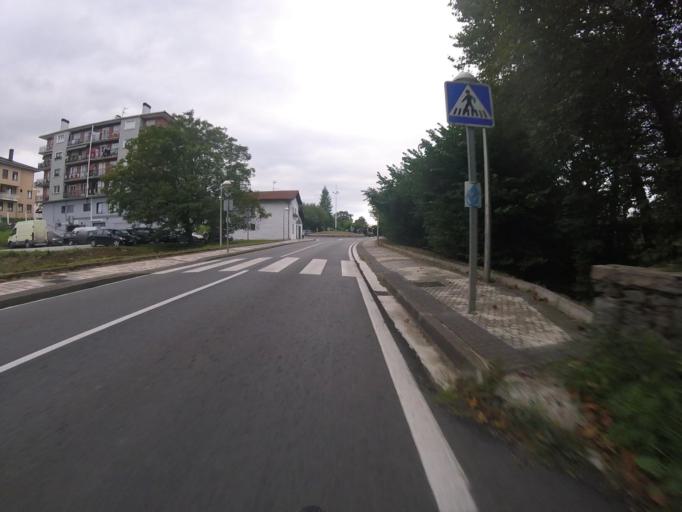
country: ES
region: Basque Country
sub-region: Provincia de Guipuzcoa
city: Errenteria
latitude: 43.2927
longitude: -1.8645
